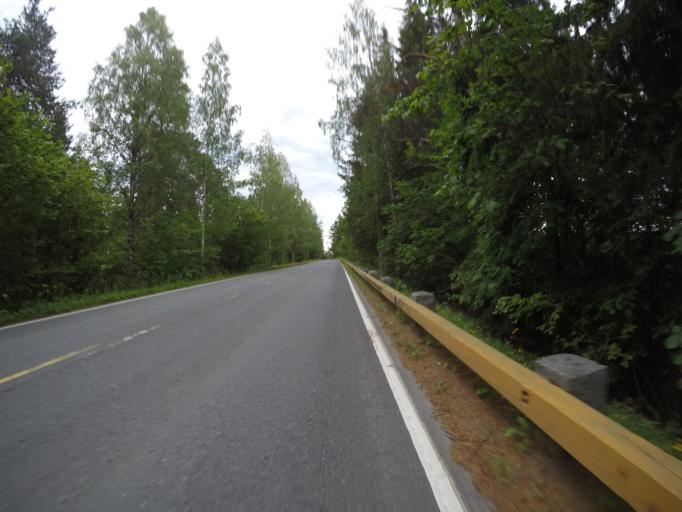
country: FI
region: Haeme
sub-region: Haemeenlinna
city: Haemeenlinna
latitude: 60.9738
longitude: 24.4673
